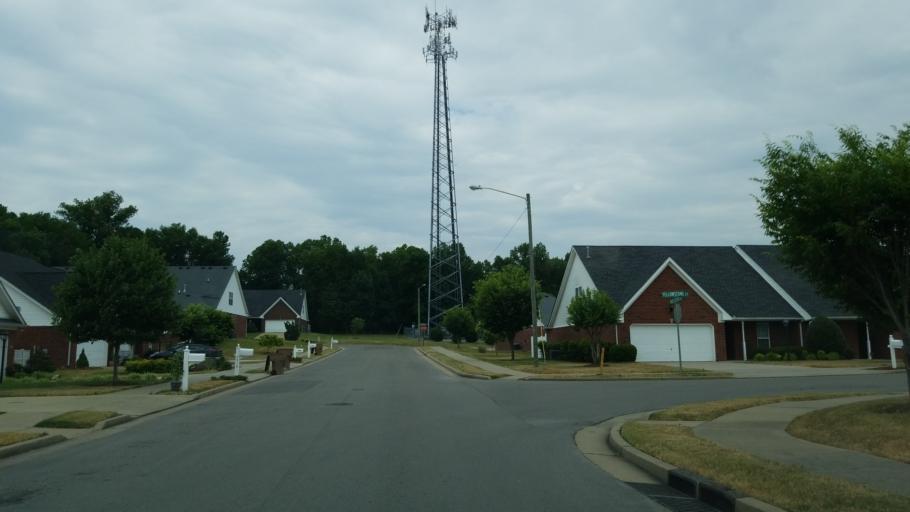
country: US
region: Tennessee
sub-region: Rutherford County
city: La Vergne
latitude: 36.0344
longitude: -86.5925
